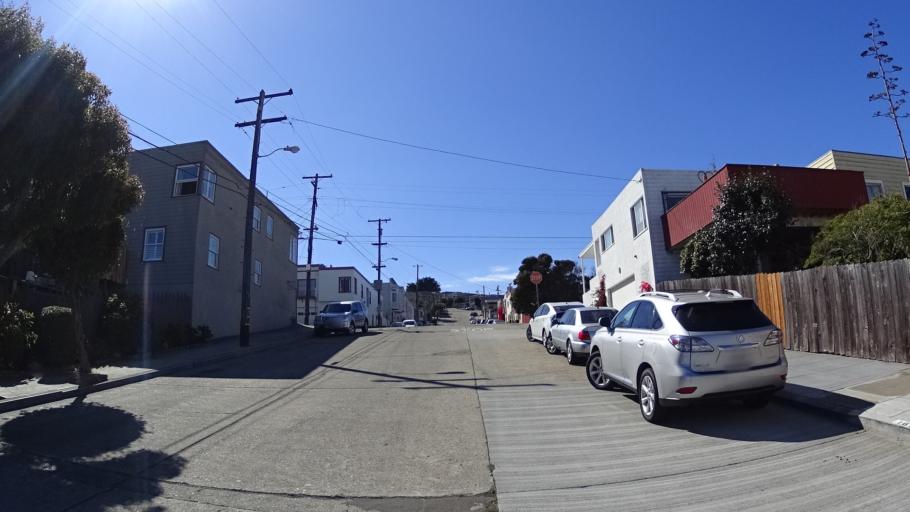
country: US
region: California
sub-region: San Mateo County
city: Daly City
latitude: 37.7270
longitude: -122.4214
